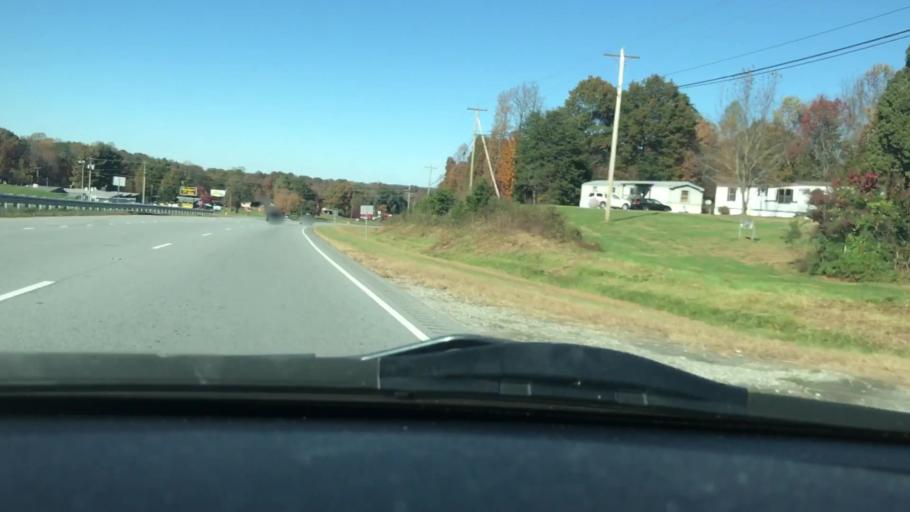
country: US
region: North Carolina
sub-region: Rockingham County
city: Madison
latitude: 36.3531
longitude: -79.9462
